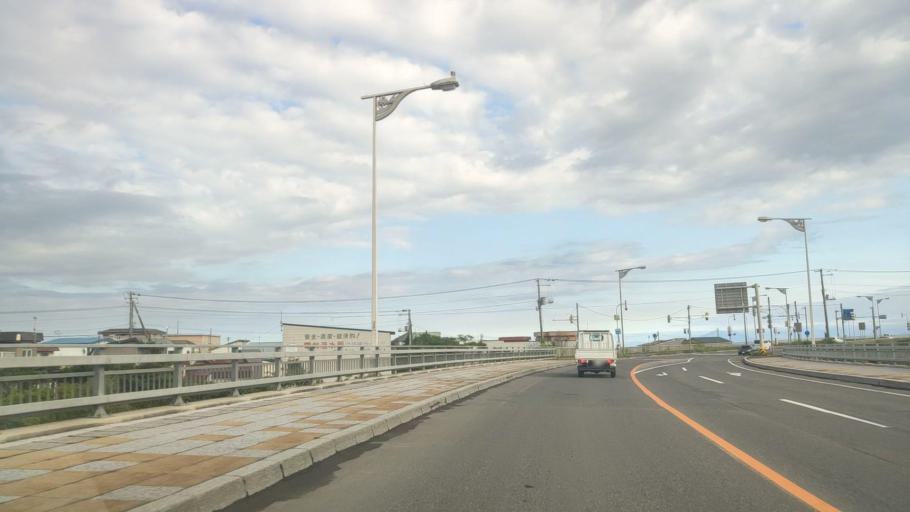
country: JP
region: Hokkaido
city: Niseko Town
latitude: 42.5175
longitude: 140.3818
